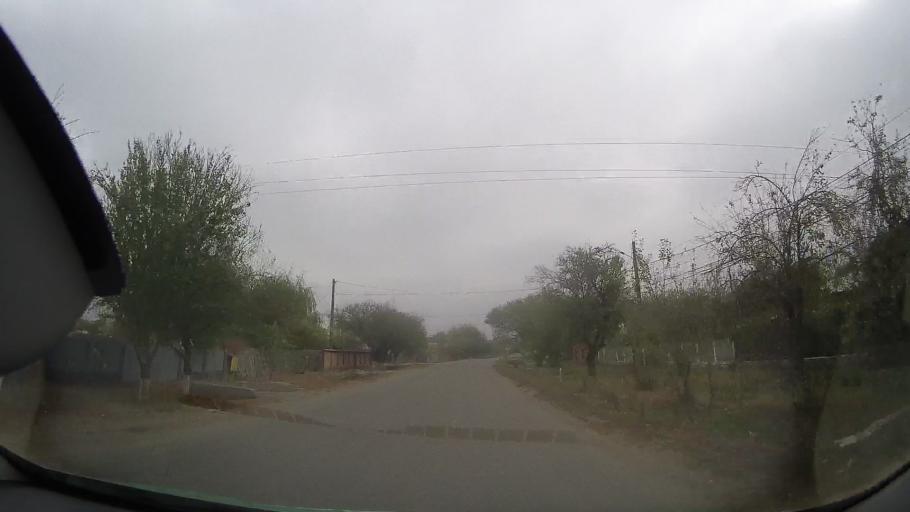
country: RO
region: Buzau
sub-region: Comuna Glodeanu-Silistea
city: Glodeanu-Silistea
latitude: 44.8209
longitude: 26.8337
